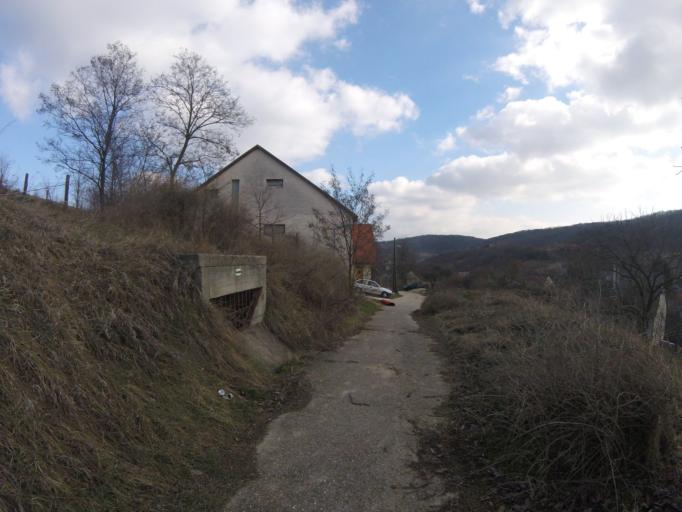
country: HU
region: Komarom-Esztergom
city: Nyergesujfalu
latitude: 47.7301
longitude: 18.5970
